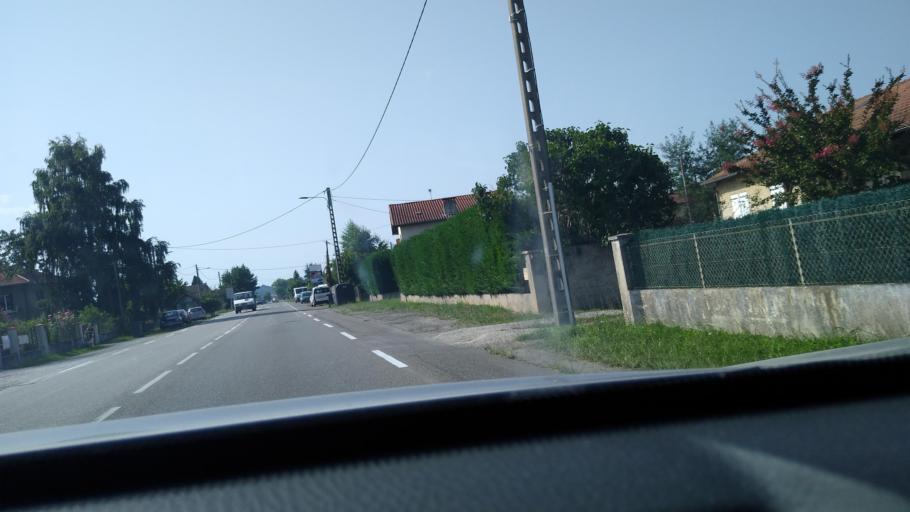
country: FR
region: Midi-Pyrenees
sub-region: Departement de l'Ariege
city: Saint-Lizier
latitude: 43.0122
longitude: 1.1145
